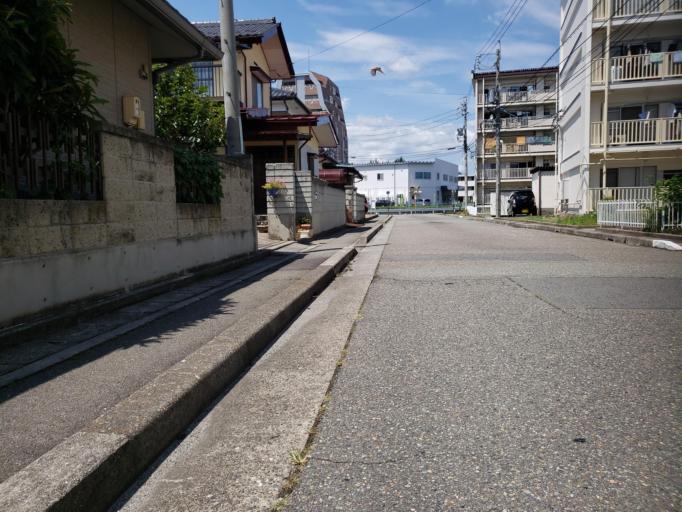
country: JP
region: Nagano
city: Nagano-shi
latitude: 36.6273
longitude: 138.1889
